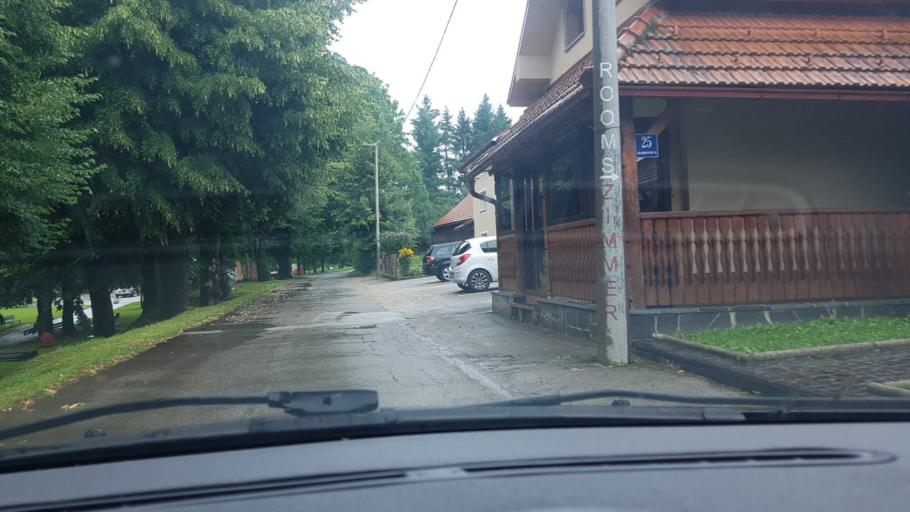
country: HR
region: Licko-Senjska
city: Jezerce
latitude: 44.9923
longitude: 15.6512
